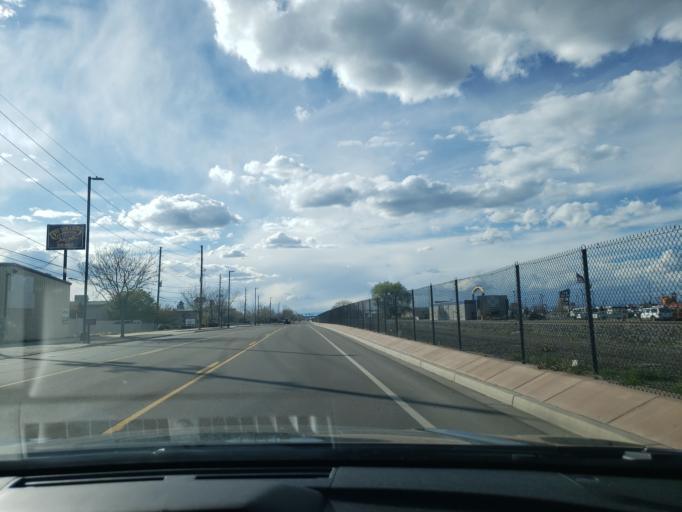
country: US
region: Colorado
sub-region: Mesa County
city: Redlands
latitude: 39.0829
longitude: -108.5933
